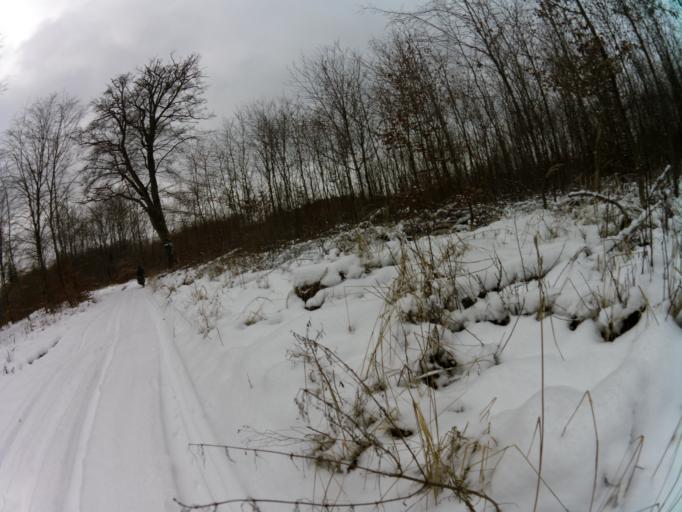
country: PL
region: West Pomeranian Voivodeship
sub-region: Powiat choszczenski
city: Recz
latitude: 53.3264
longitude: 15.5437
